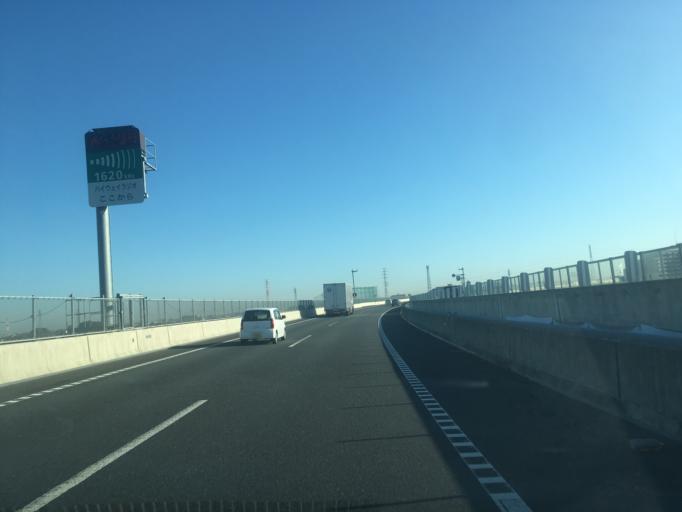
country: JP
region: Saitama
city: Satte
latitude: 36.0633
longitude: 139.7013
